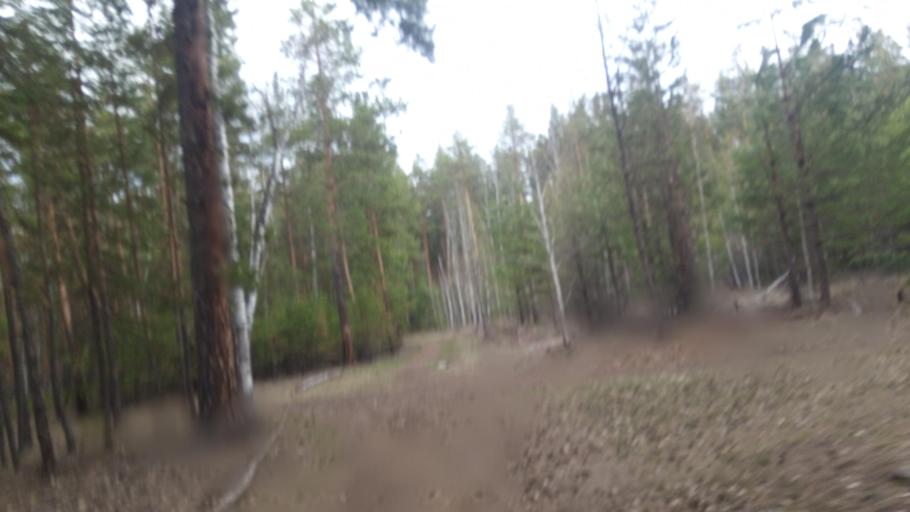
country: RU
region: Chelyabinsk
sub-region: Gorod Chelyabinsk
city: Chelyabinsk
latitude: 55.1342
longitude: 61.3372
